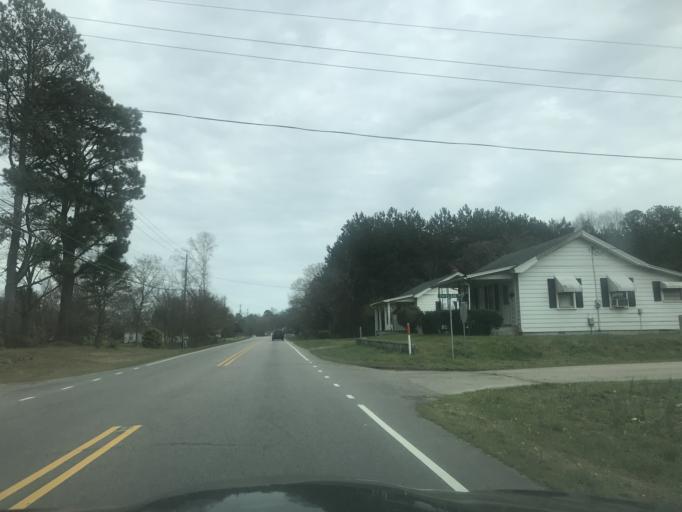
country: US
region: North Carolina
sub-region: Franklin County
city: Franklinton
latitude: 36.1041
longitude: -78.4453
